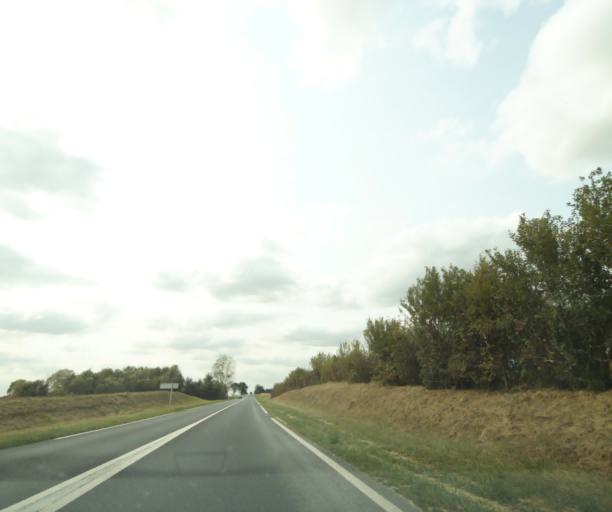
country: FR
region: Centre
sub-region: Departement de l'Indre
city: Buzancais
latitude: 46.9058
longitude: 1.3522
